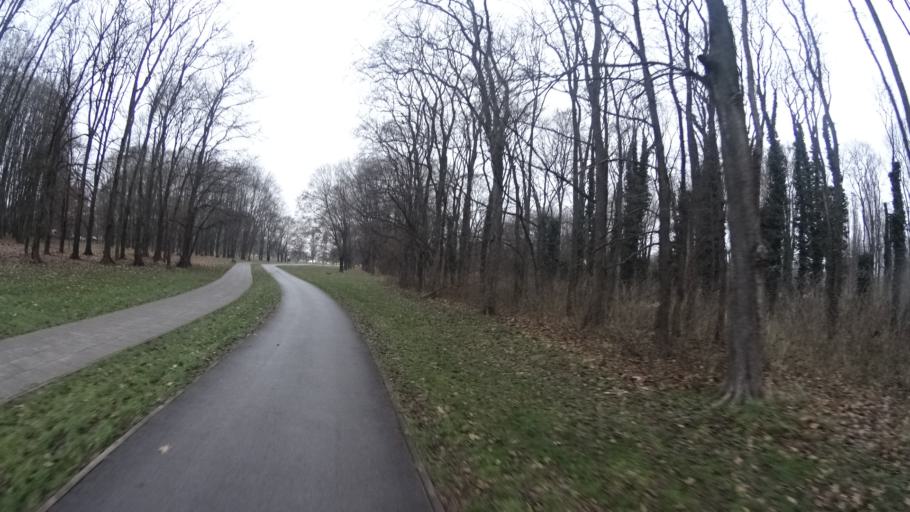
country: PL
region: Masovian Voivodeship
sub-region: Warszawa
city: Ochota
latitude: 52.2099
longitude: 20.9934
